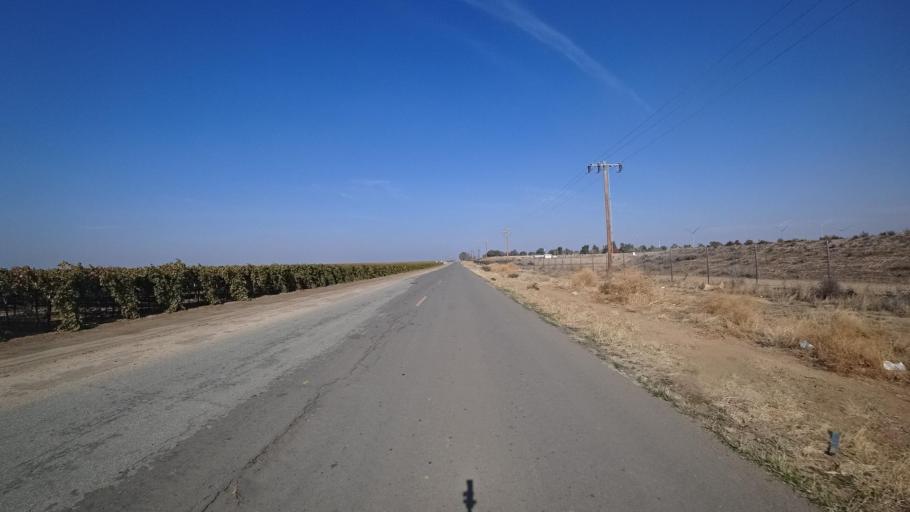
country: US
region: California
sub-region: Kern County
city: Greenacres
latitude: 35.5095
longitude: -119.1166
